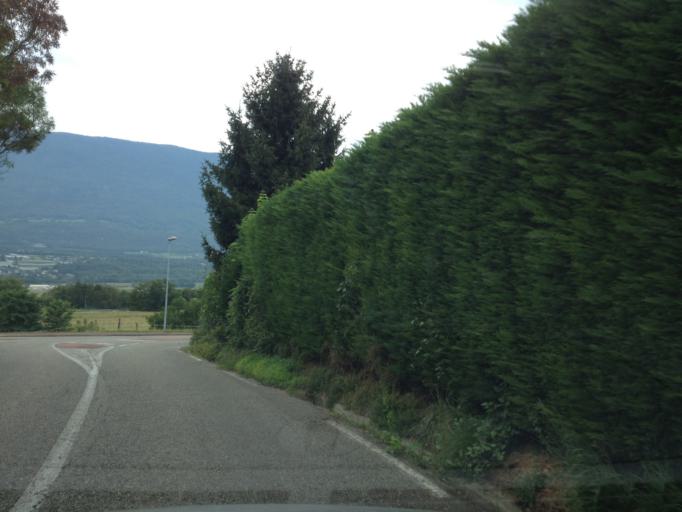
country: FR
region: Rhone-Alpes
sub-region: Departement de la Savoie
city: Voglans
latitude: 45.6237
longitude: 5.9031
